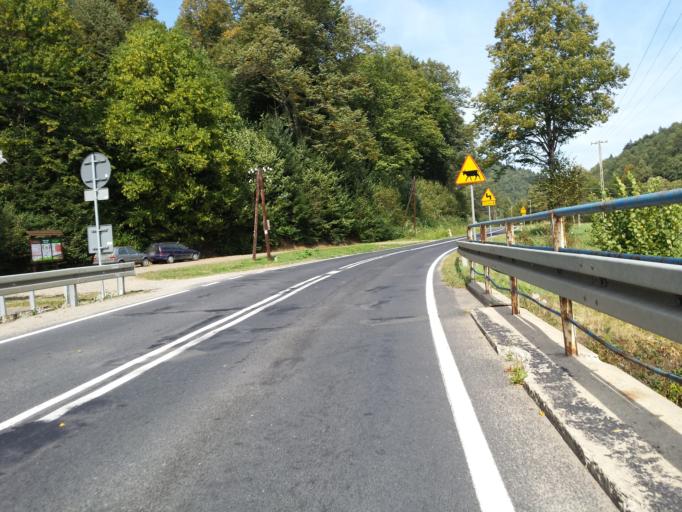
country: PL
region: Subcarpathian Voivodeship
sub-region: Powiat leski
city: Baligrod
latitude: 49.3616
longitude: 22.2763
